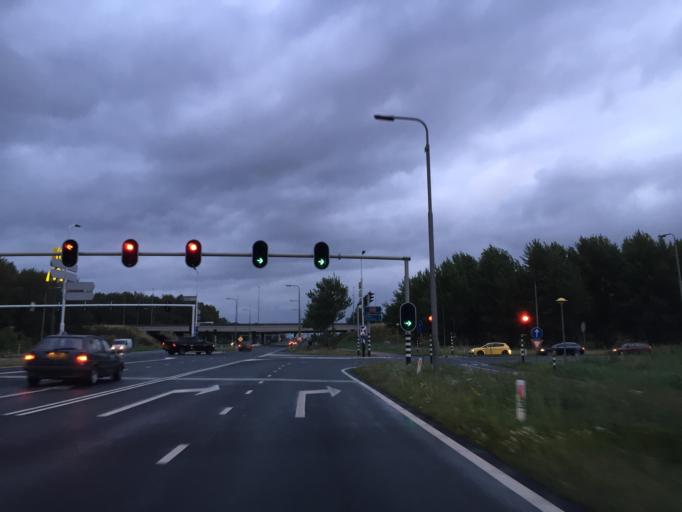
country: NL
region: Flevoland
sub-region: Gemeente Lelystad
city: Lelystad
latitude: 52.4818
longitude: 5.5008
